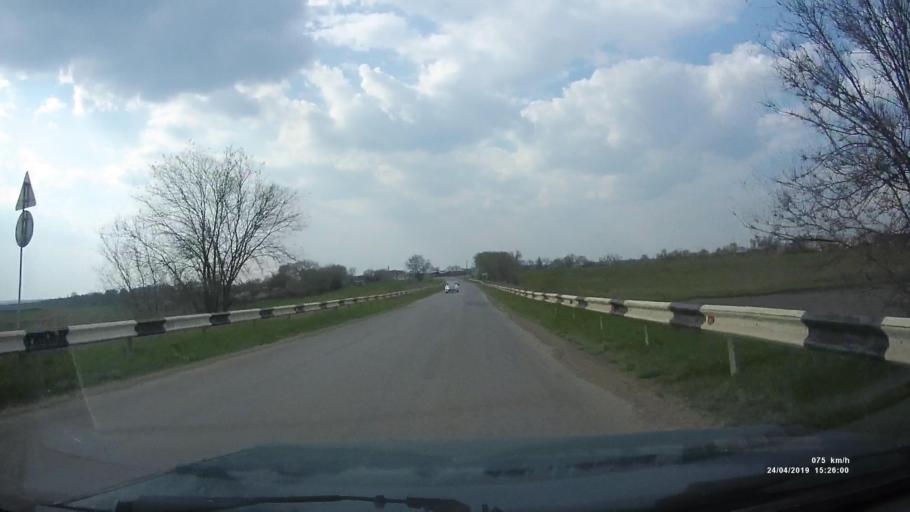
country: RU
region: Rostov
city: Remontnoye
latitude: 46.5556
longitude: 43.0385
